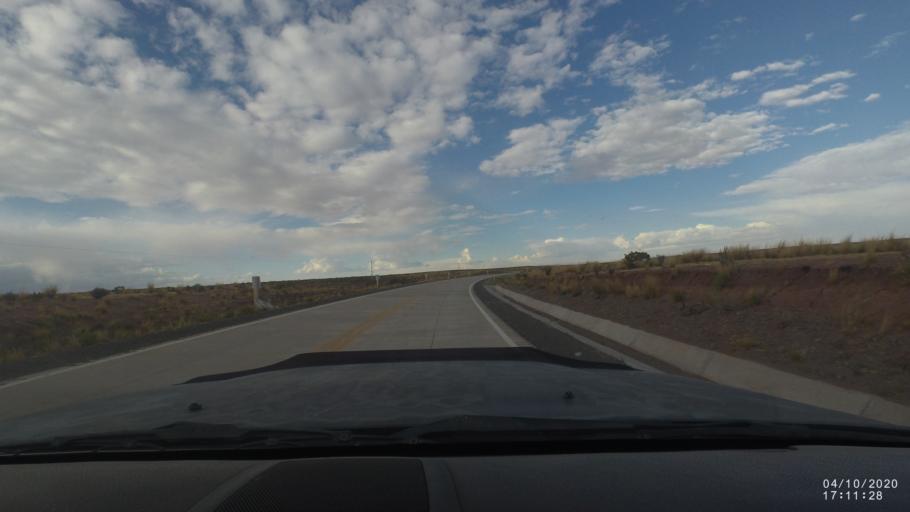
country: BO
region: Oruro
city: Oruro
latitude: -18.3195
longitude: -67.5762
